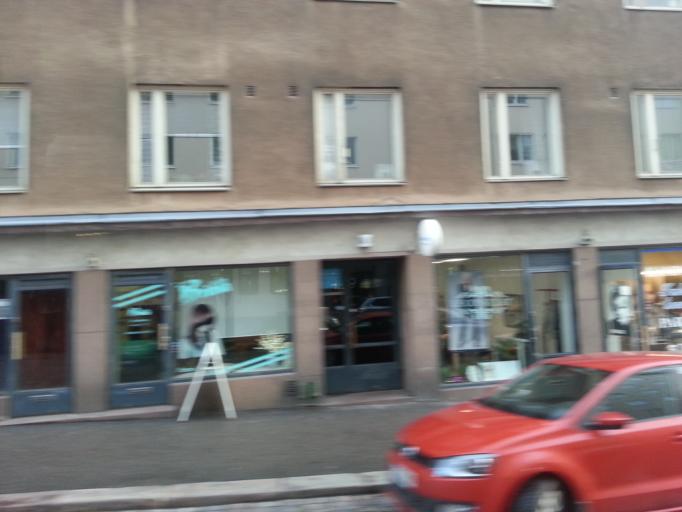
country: FI
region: Uusimaa
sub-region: Helsinki
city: Helsinki
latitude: 60.1821
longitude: 24.9514
